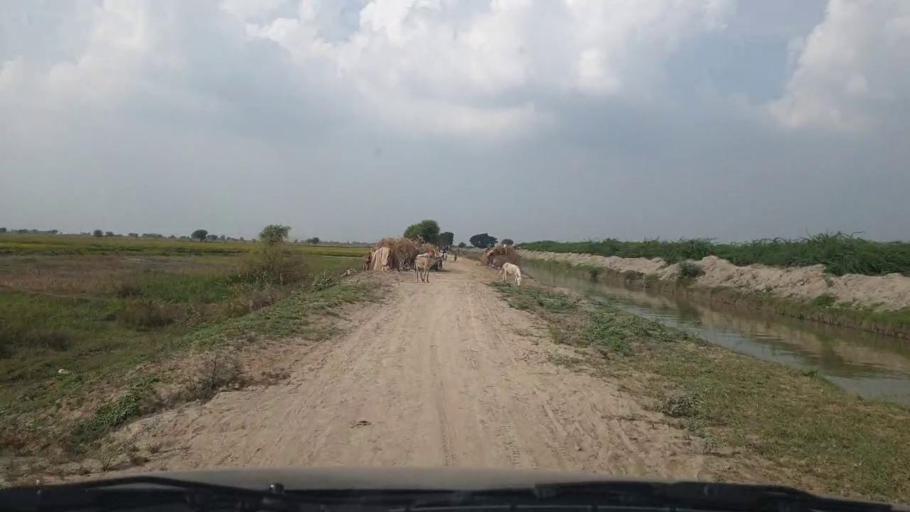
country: PK
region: Sindh
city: Badin
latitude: 24.5727
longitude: 68.6308
